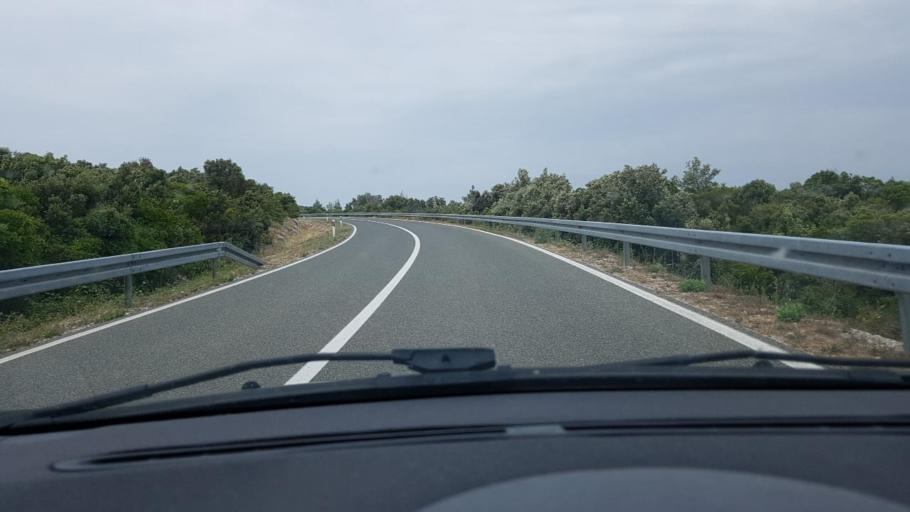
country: HR
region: Dubrovacko-Neretvanska
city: Smokvica
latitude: 42.9476
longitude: 16.9529
